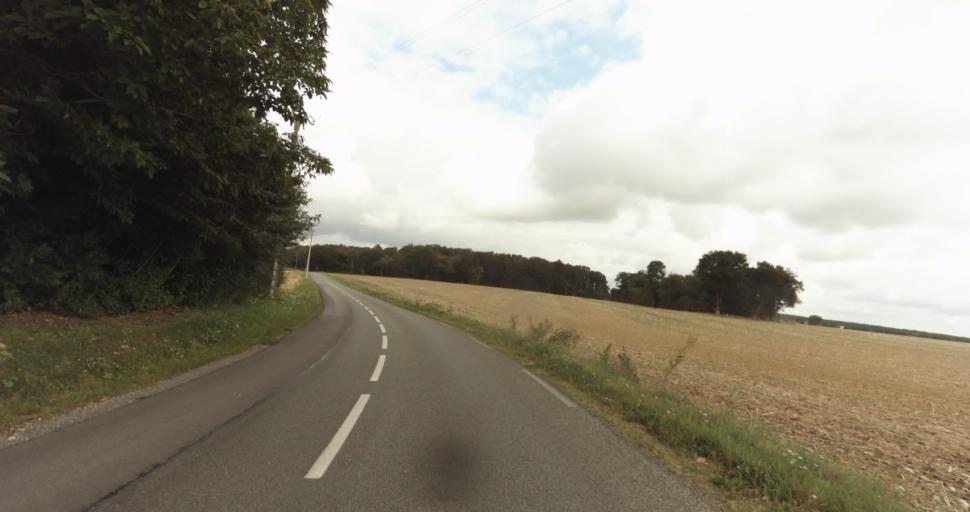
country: FR
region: Haute-Normandie
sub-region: Departement de l'Eure
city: Menilles
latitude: 48.9788
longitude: 1.2782
